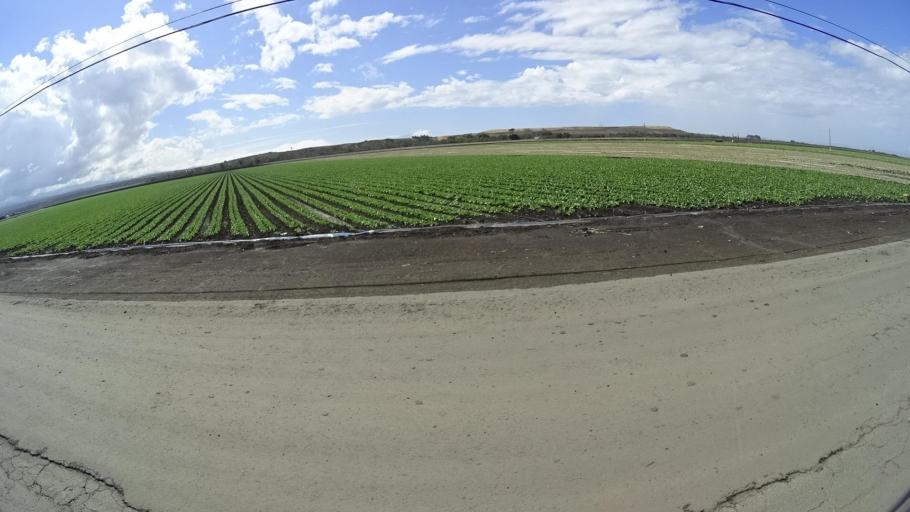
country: US
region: California
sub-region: Monterey County
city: Castroville
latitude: 36.7092
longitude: -121.7382
